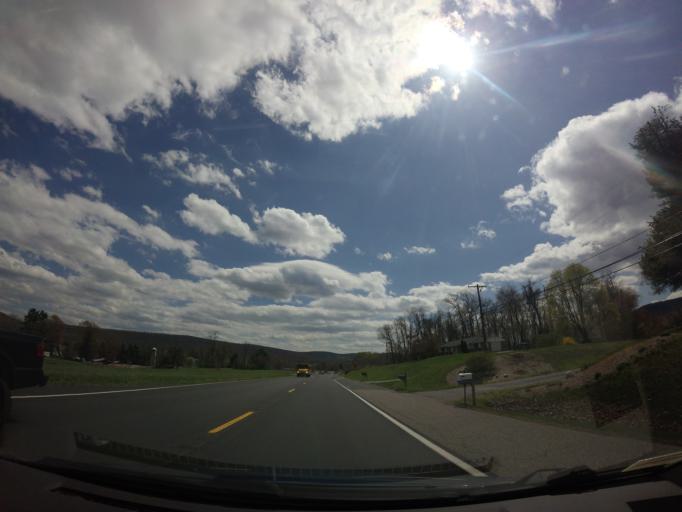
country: US
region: Maryland
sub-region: Washington County
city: Keedysville
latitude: 39.4132
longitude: -77.6625
